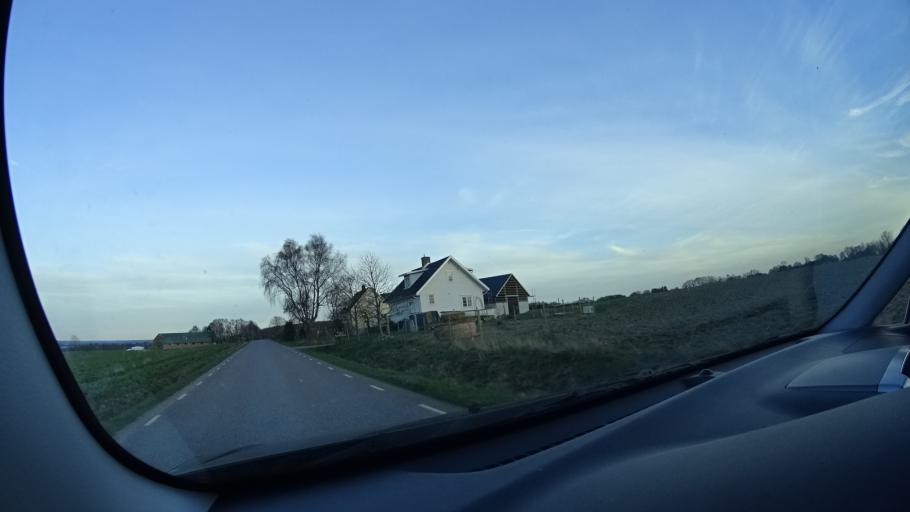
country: SE
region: Skane
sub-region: Eslovs Kommun
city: Stehag
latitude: 55.8831
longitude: 13.4348
